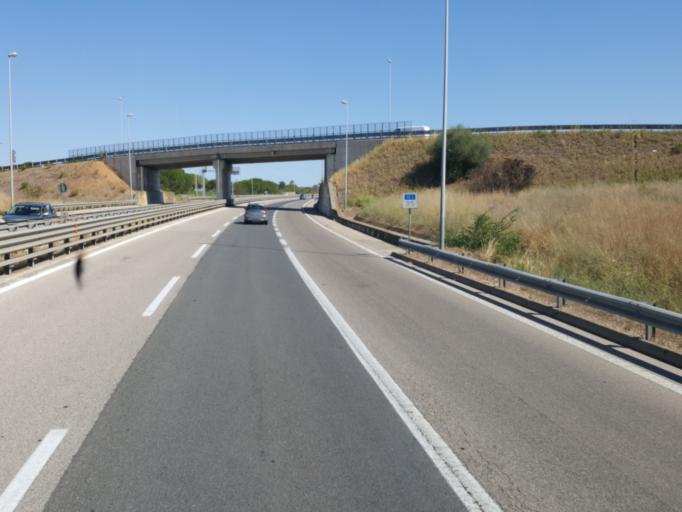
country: IT
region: Tuscany
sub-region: Provincia di Grosseto
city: Grosseto
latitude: 42.7303
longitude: 11.1359
